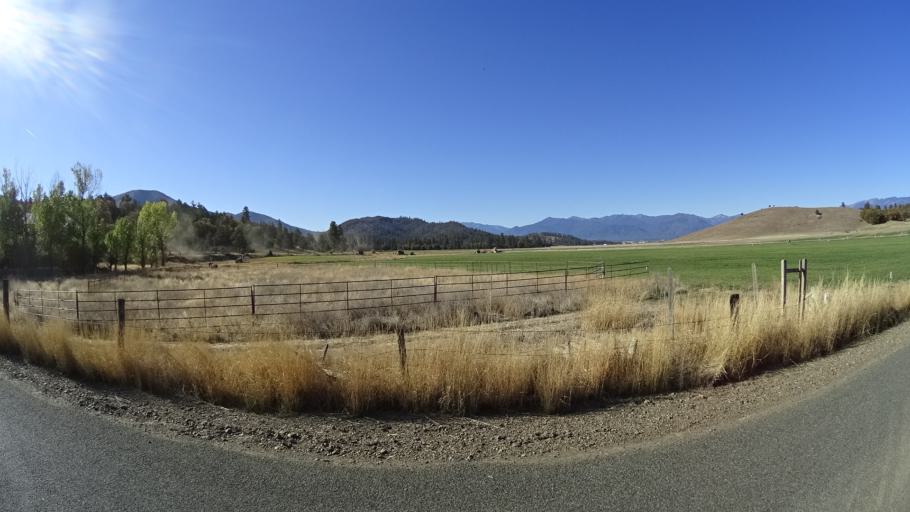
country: US
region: California
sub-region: Siskiyou County
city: Yreka
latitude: 41.5791
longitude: -122.7892
